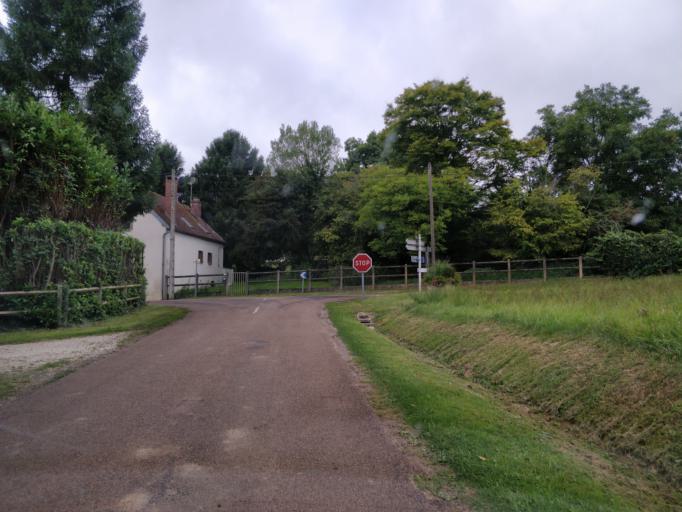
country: FR
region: Bourgogne
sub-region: Departement de l'Yonne
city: Neuvy-Sautour
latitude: 48.1214
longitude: 3.8402
